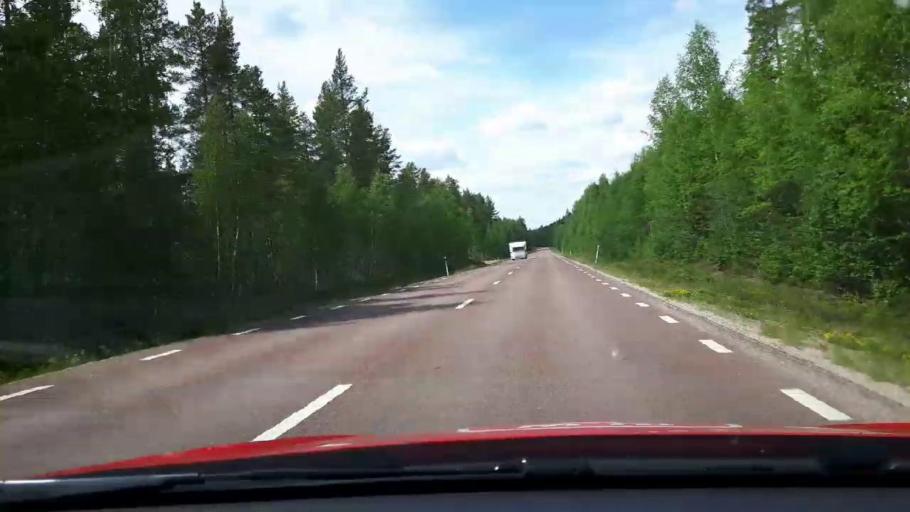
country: SE
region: Jaemtland
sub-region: Harjedalens Kommun
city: Sveg
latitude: 62.0452
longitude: 14.8535
